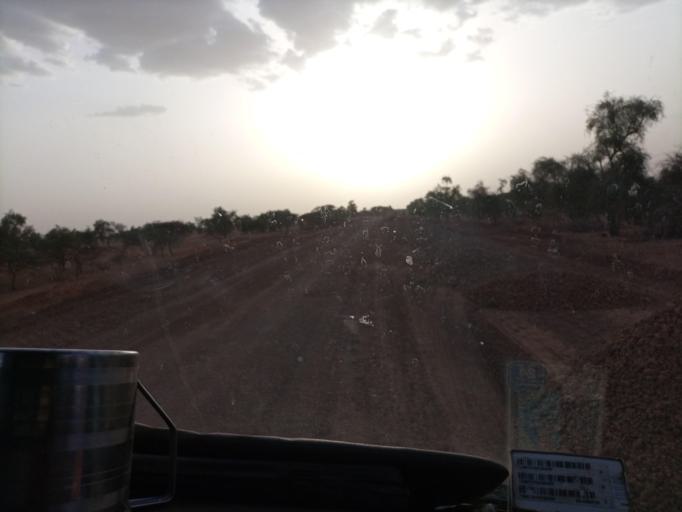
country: SN
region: Louga
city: Dara
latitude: 15.3838
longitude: -15.6202
